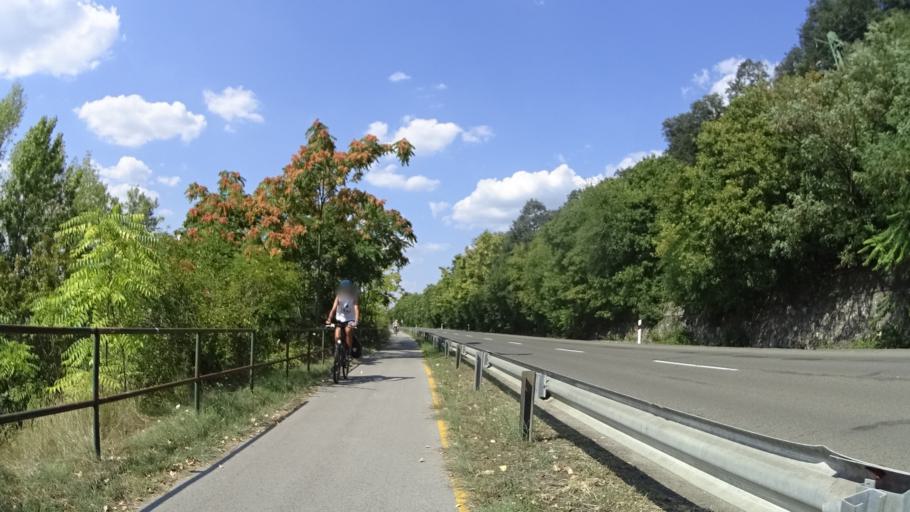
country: HU
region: Komarom-Esztergom
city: Pilismarot
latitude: 47.7773
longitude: 18.9132
